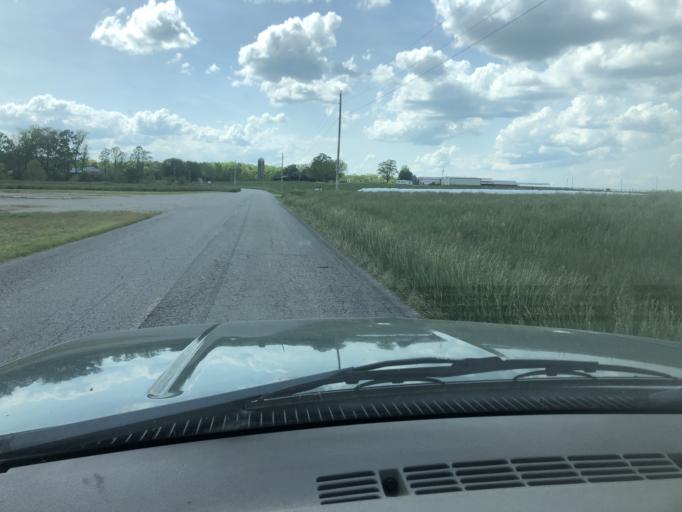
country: US
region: Tennessee
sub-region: Fentress County
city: Jamestown
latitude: 36.3158
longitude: -84.8599
